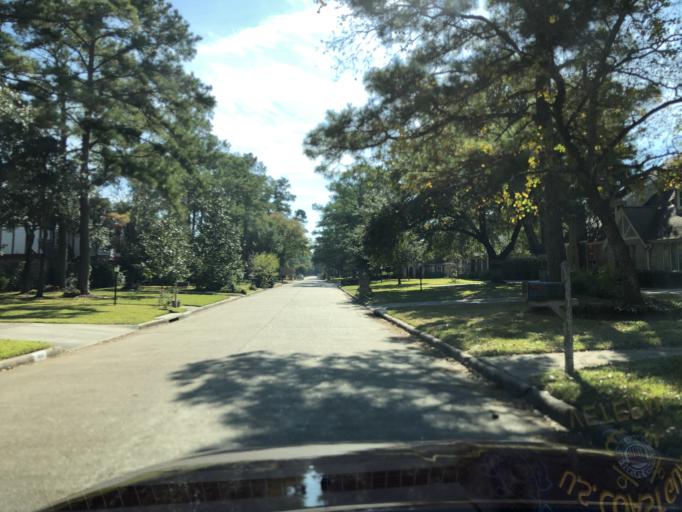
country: US
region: Texas
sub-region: Harris County
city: Tomball
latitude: 30.0252
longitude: -95.5529
